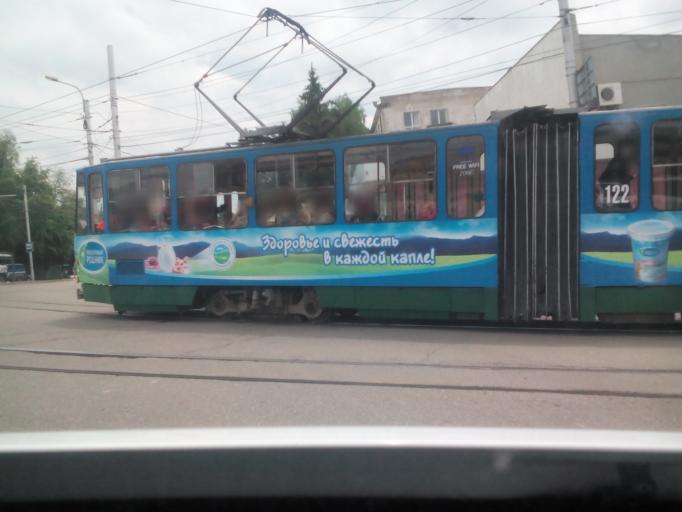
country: RU
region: Stavropol'skiy
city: Pyatigorsk
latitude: 44.0531
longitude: 43.0628
